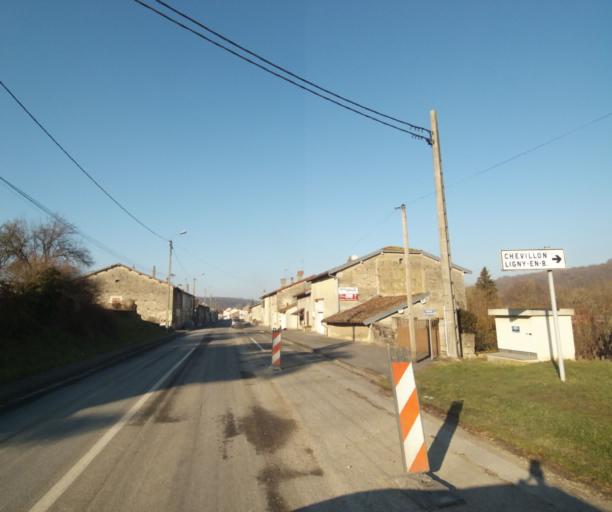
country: FR
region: Champagne-Ardenne
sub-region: Departement de la Haute-Marne
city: Chevillon
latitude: 48.5222
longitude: 5.1045
